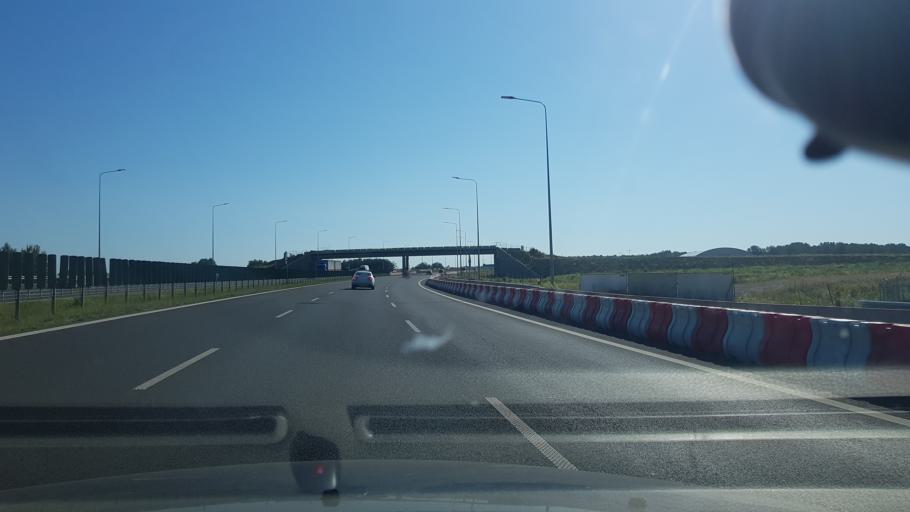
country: PL
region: Masovian Voivodeship
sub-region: Powiat wolominski
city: Slupno
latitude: 52.3514
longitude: 21.1627
